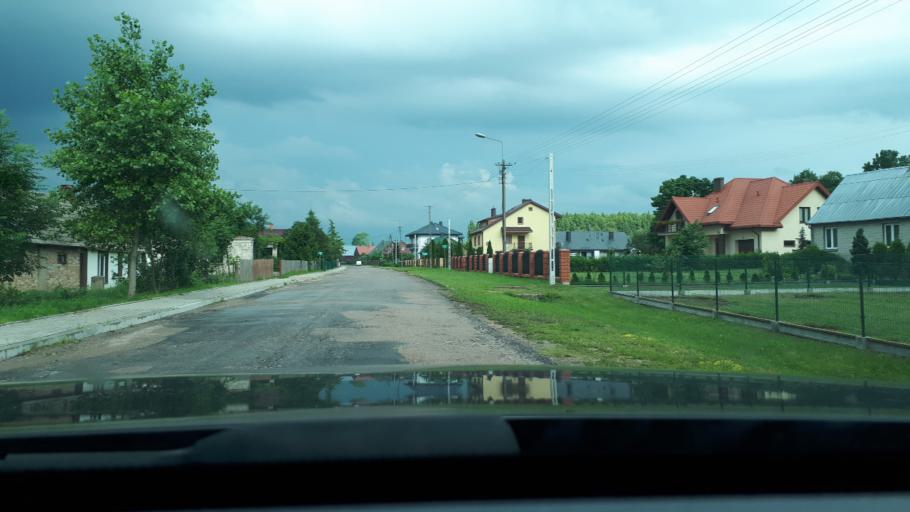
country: PL
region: Podlasie
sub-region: Powiat moniecki
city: Knyszyn
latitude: 53.2734
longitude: 22.9771
